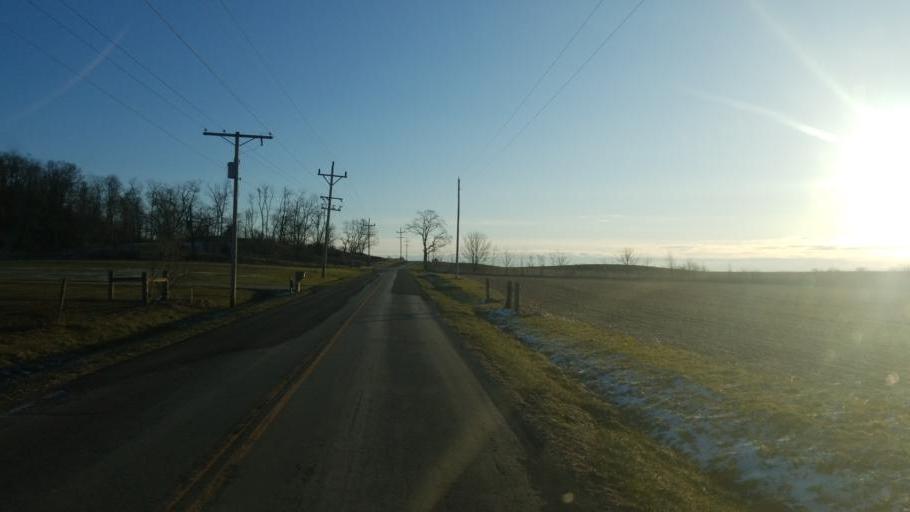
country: US
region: Ohio
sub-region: Highland County
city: Leesburg
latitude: 39.2543
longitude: -83.4694
